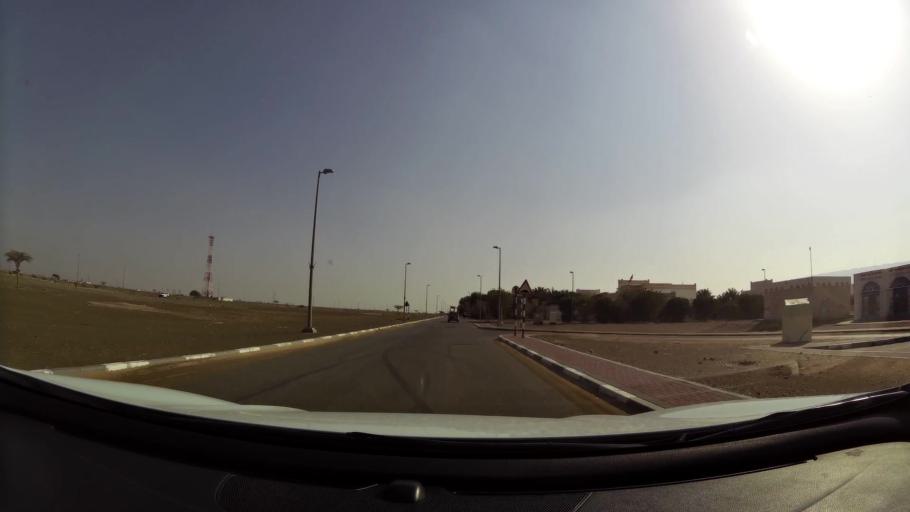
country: AE
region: Abu Dhabi
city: Al Ain
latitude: 24.0850
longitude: 55.8728
